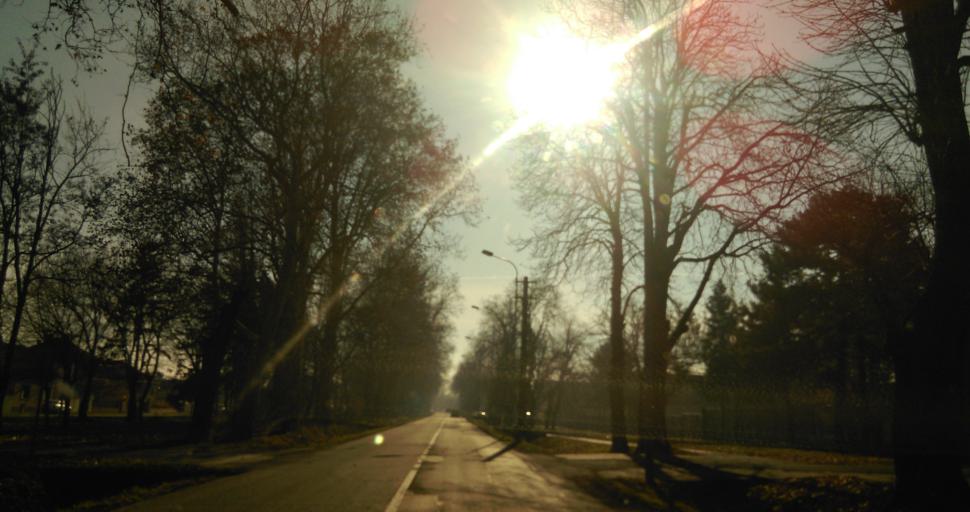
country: RS
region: Autonomna Pokrajina Vojvodina
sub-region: Sremski Okrug
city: Ruma
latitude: 44.9993
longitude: 19.8233
